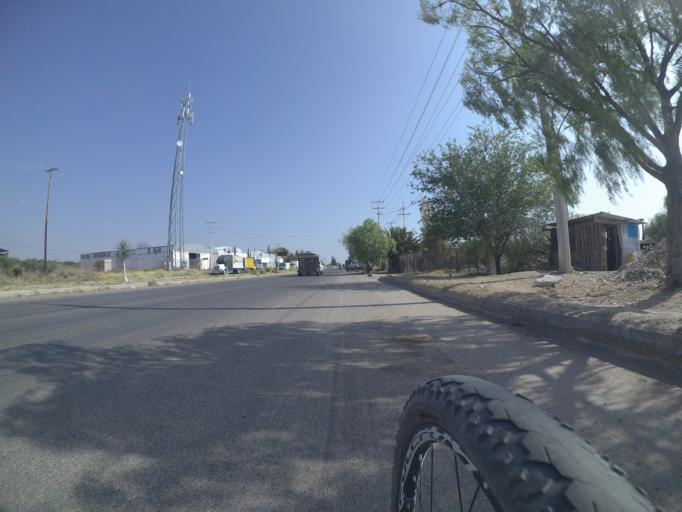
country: MX
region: Aguascalientes
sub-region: Jesus Maria
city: Paseos de las Haciendas [Fraccionamiento]
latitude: 21.9905
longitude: -102.3341
